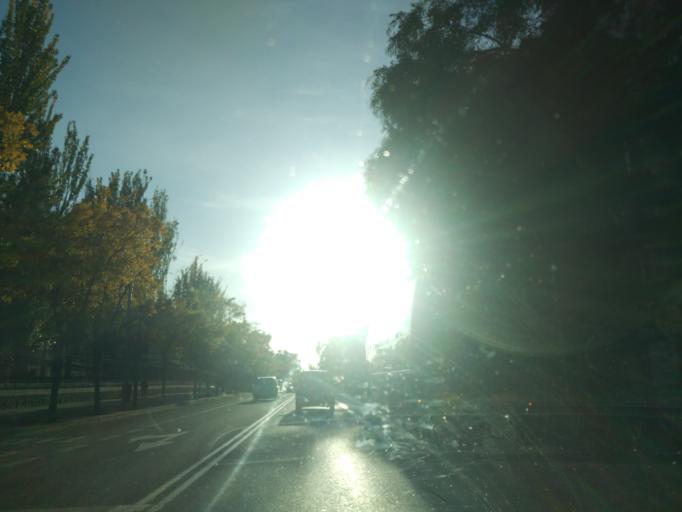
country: ES
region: Madrid
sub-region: Provincia de Madrid
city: Latina
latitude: 40.3864
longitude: -3.7350
